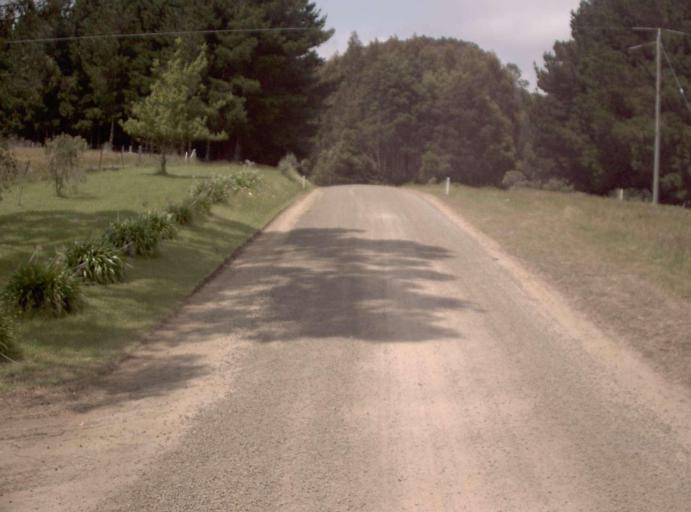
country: AU
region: Victoria
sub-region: Latrobe
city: Traralgon
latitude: -38.4156
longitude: 146.6165
